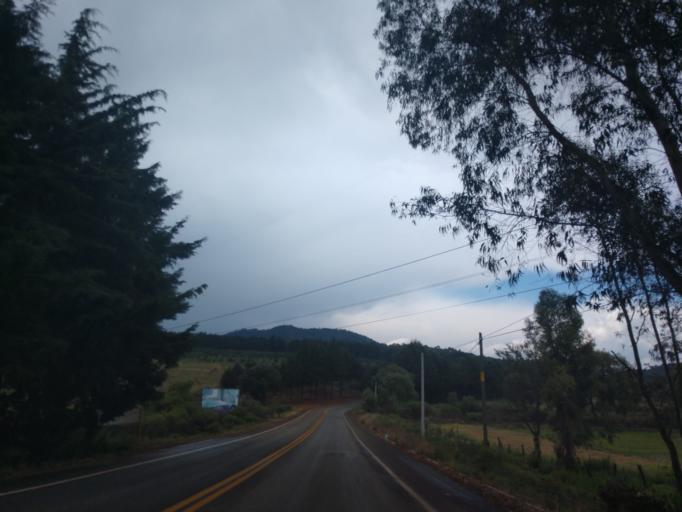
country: MX
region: Jalisco
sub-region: Mazamitla
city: Mazamitla
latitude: 19.9363
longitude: -103.0542
